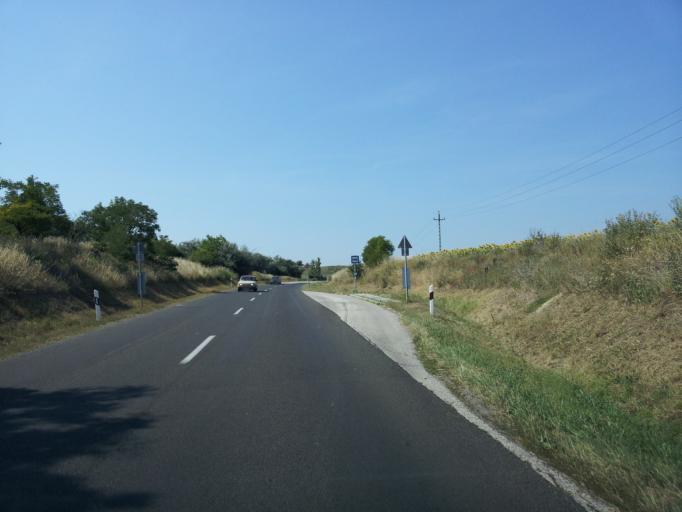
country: HU
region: Fejer
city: Lovasbereny
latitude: 47.2671
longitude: 18.5257
